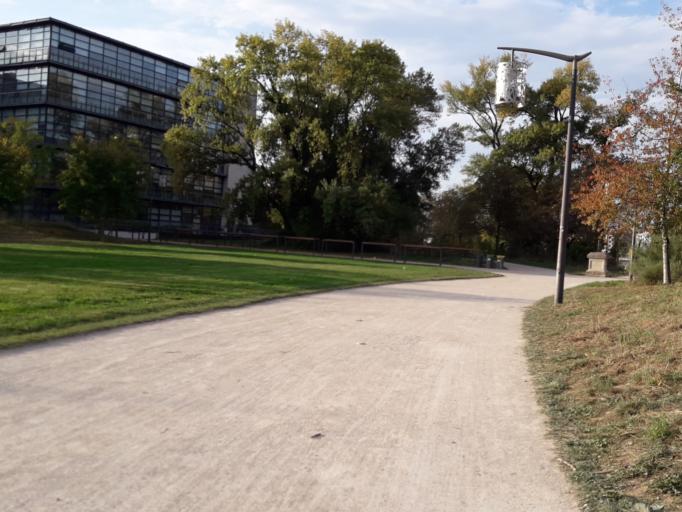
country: FR
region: Rhone-Alpes
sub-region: Departement du Rhone
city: La Mulatiere
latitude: 45.7297
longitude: 4.8216
